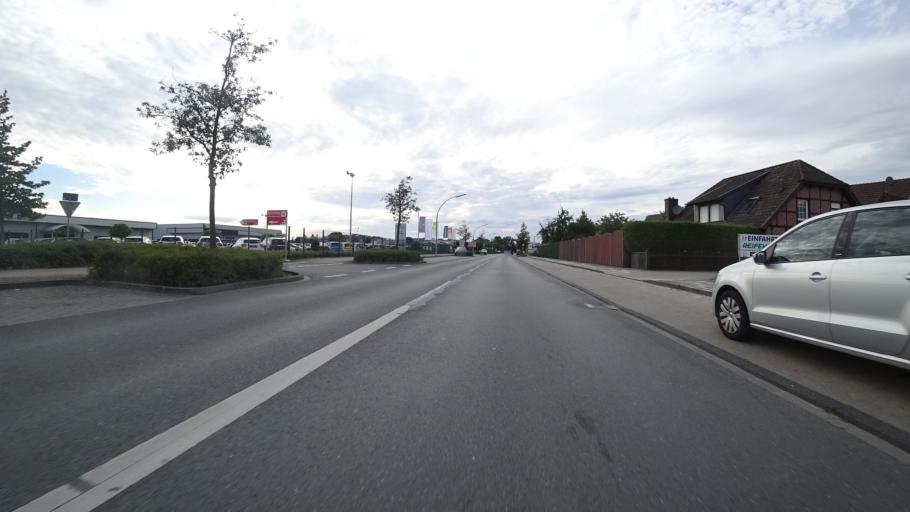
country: DE
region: North Rhine-Westphalia
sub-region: Regierungsbezirk Munster
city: Warendorf
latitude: 51.9430
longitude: 8.0079
